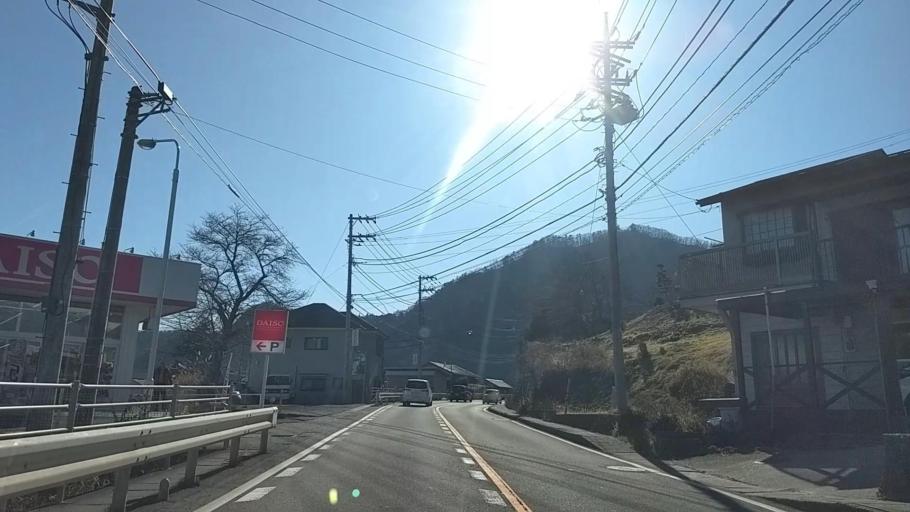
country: JP
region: Yamanashi
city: Uenohara
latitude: 35.6193
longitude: 139.1074
